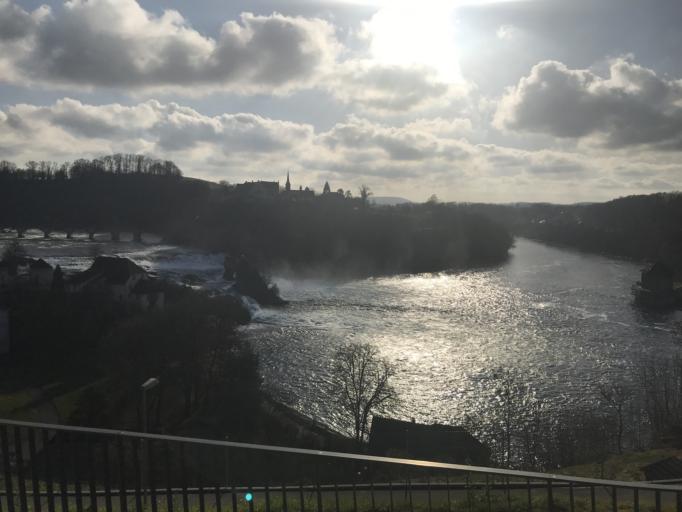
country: CH
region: Schaffhausen
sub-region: Bezirk Schaffhausen
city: Neuhausen
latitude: 47.6806
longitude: 8.6145
